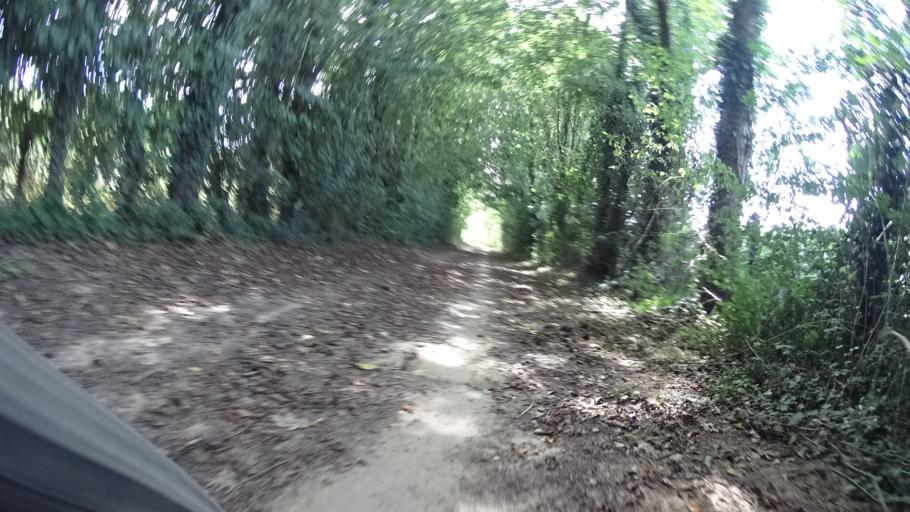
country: FR
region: Brittany
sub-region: Departement d'Ille-et-Vilaine
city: La Meziere
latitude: 48.2236
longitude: -1.7343
